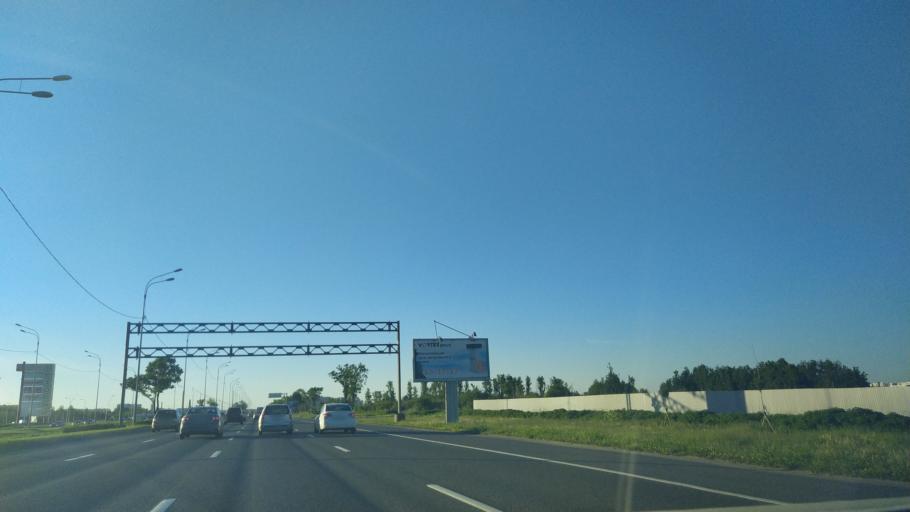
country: RU
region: St.-Petersburg
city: Aleksandrovskaya
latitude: 59.7861
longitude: 30.3254
